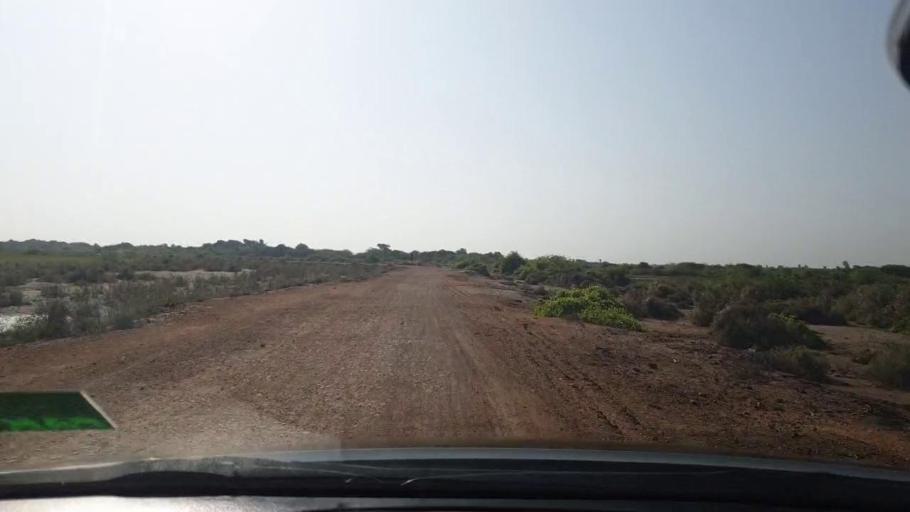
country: PK
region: Sindh
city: Tando Bago
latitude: 24.7148
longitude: 68.9709
